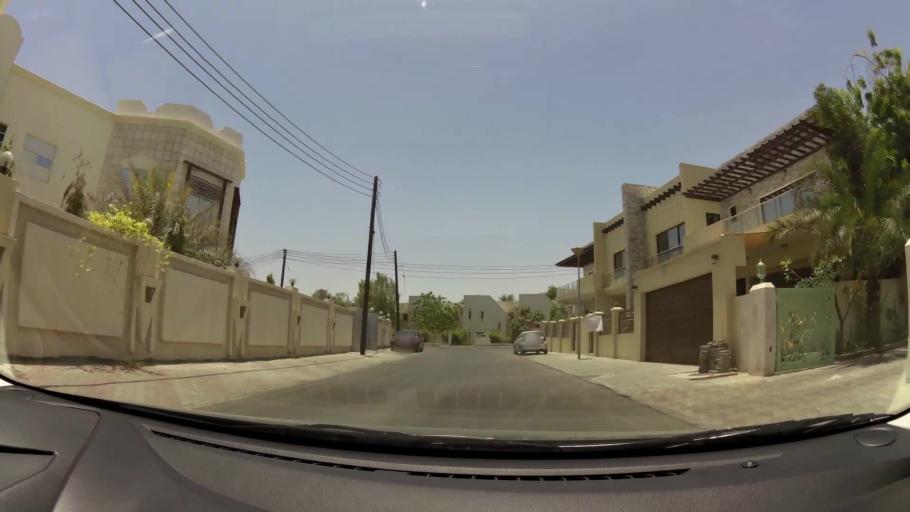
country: OM
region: Muhafazat Masqat
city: Bawshar
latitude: 23.6048
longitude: 58.4571
